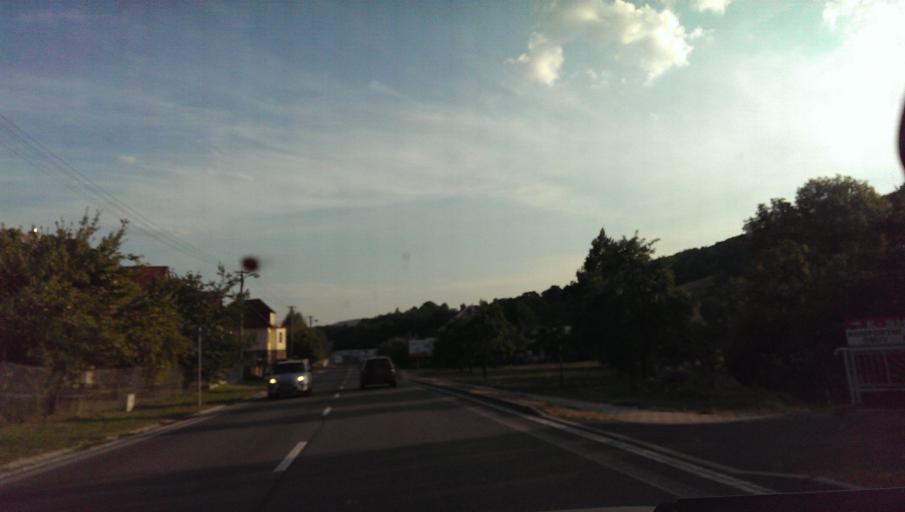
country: CZ
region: Zlin
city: Pozlovice
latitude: 49.1507
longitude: 17.8037
